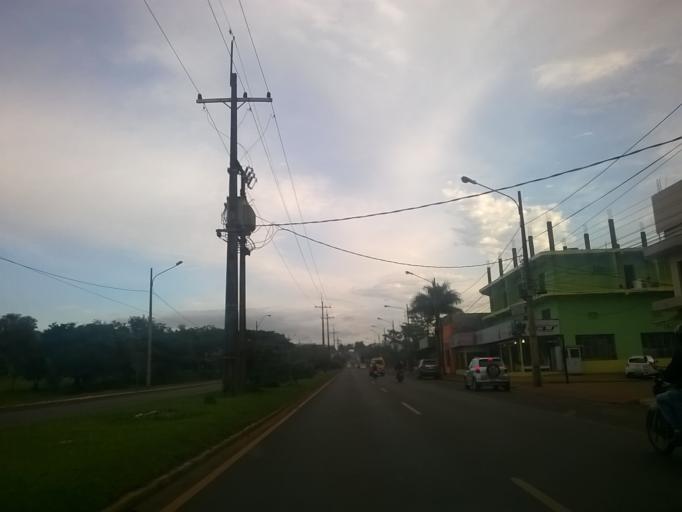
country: PY
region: Alto Parana
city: Presidente Franco
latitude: -25.5287
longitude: -54.6362
